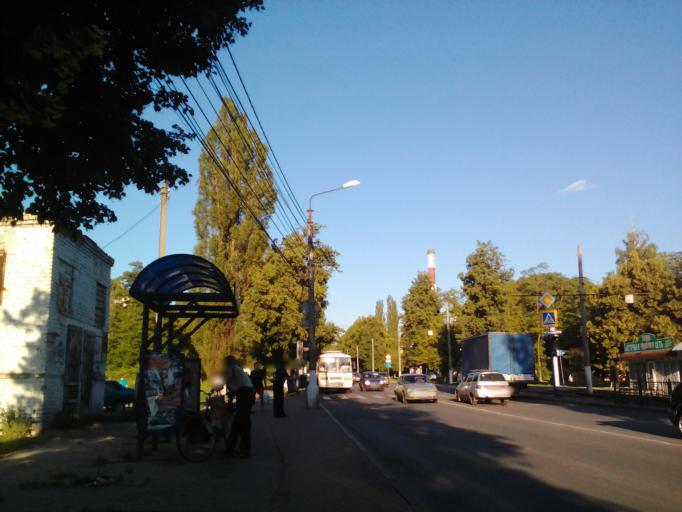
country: RU
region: Kursk
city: Voroshnevo
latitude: 51.6673
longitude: 36.1016
